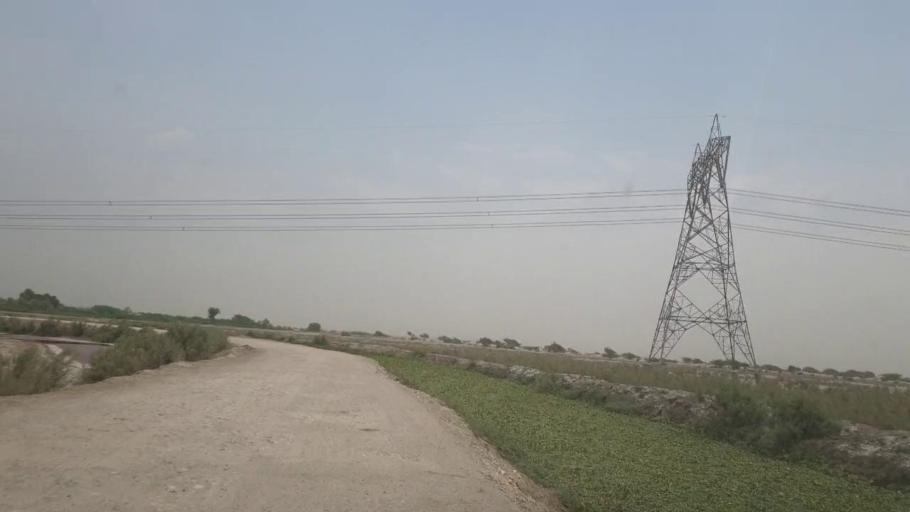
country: PK
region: Sindh
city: Kot Diji
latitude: 27.4234
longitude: 68.6842
